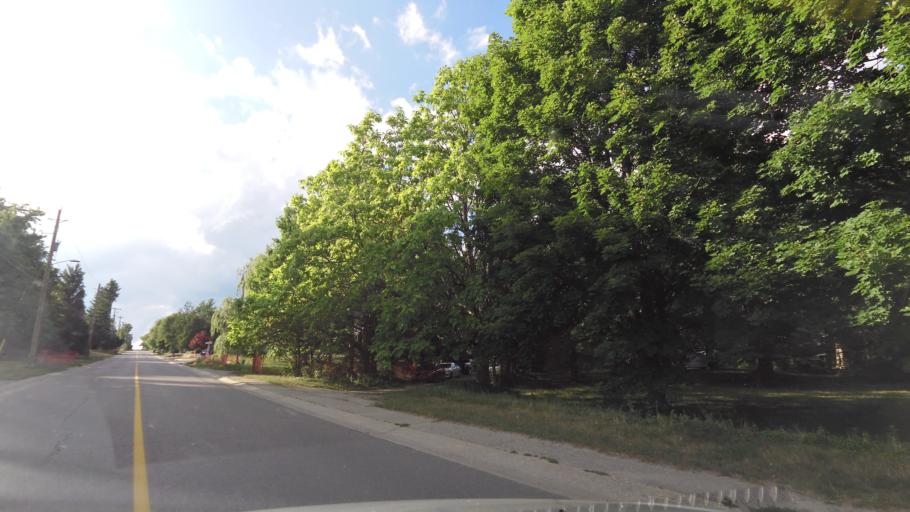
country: CA
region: Ontario
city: Brampton
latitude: 43.7571
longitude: -79.9284
